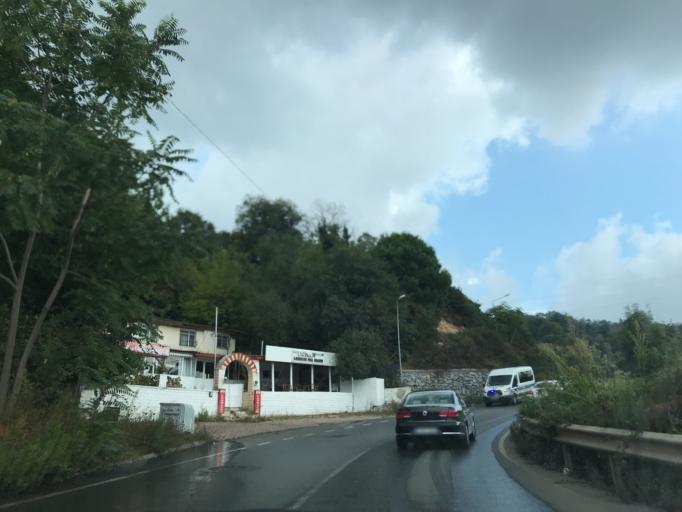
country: TR
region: Istanbul
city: Arikoey
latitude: 41.1817
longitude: 29.0455
